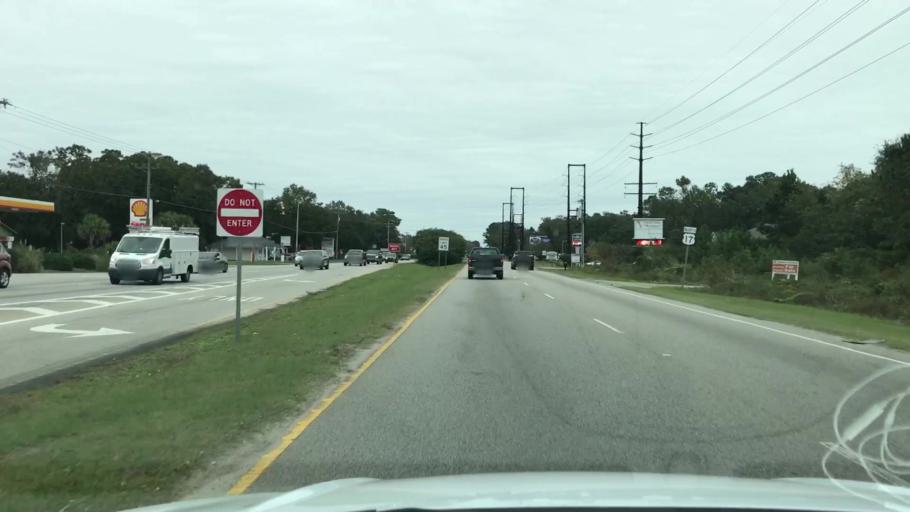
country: US
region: South Carolina
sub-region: Georgetown County
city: Murrells Inlet
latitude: 33.5498
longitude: -79.0482
